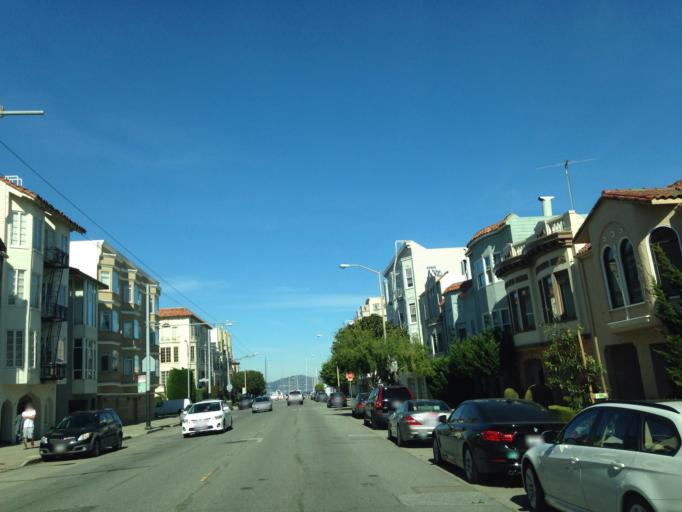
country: US
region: California
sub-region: San Francisco County
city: San Francisco
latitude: 37.8039
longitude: -122.4437
